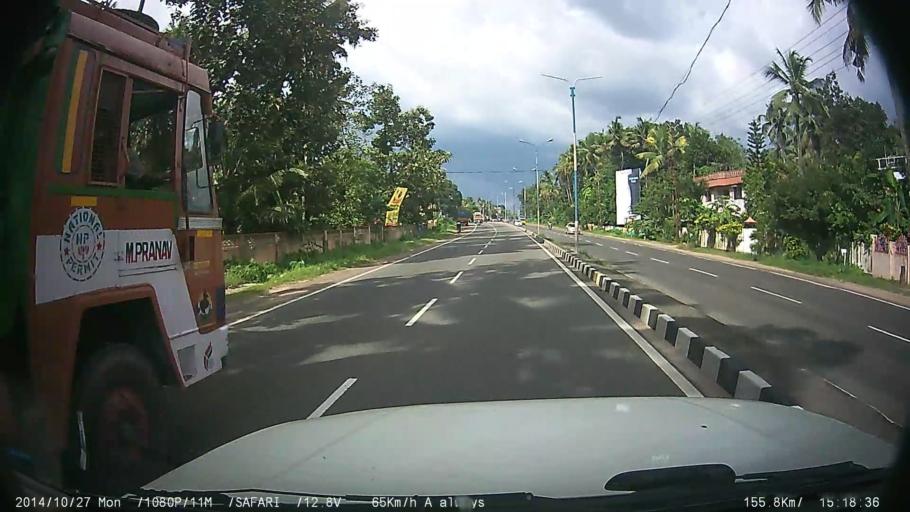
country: IN
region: Kerala
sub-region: Ernakulam
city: Angamali
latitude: 10.1669
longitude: 76.3710
